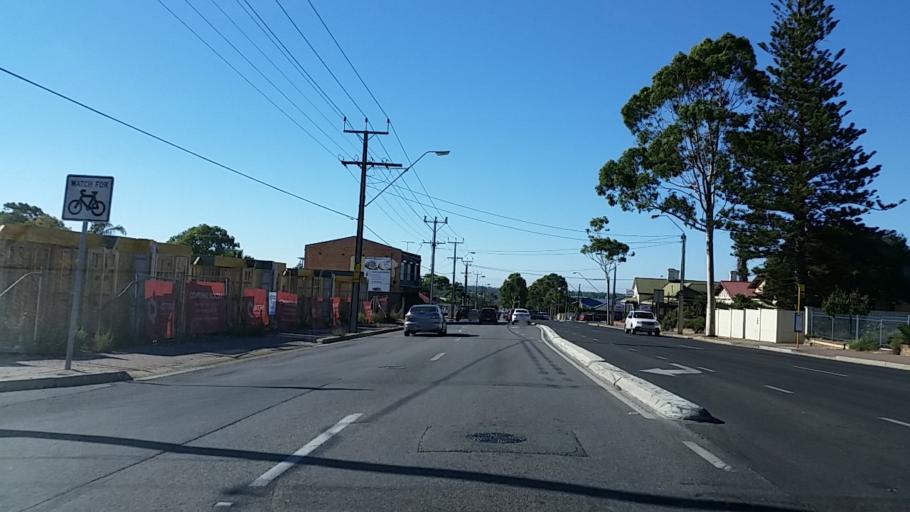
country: AU
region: South Australia
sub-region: Adelaide Hills
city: Seacliff
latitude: -35.0315
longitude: 138.5240
